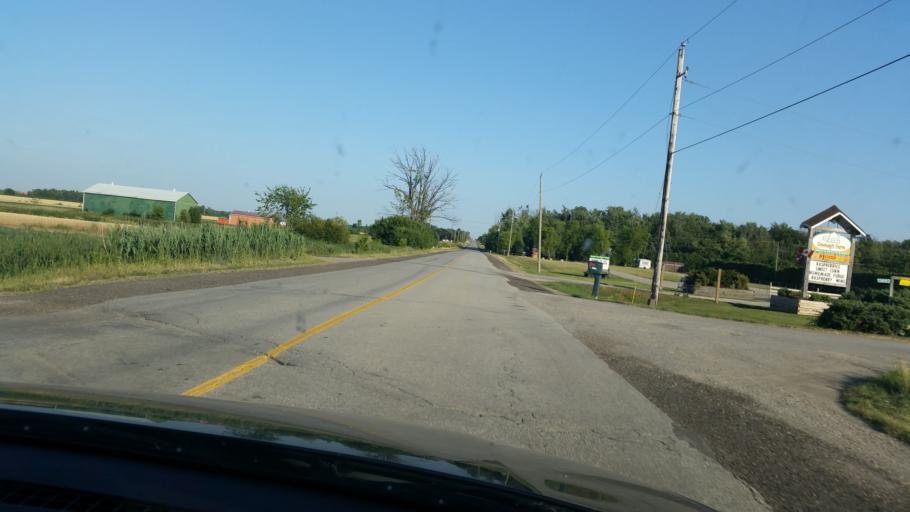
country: CA
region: Ontario
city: Brampton
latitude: 43.7863
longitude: -79.8486
